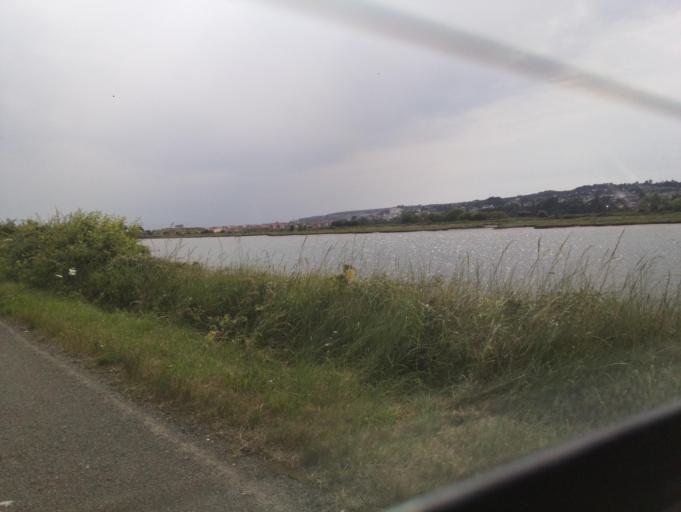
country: GB
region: England
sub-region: Devon
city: Colyton
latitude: 50.7130
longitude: -3.0560
